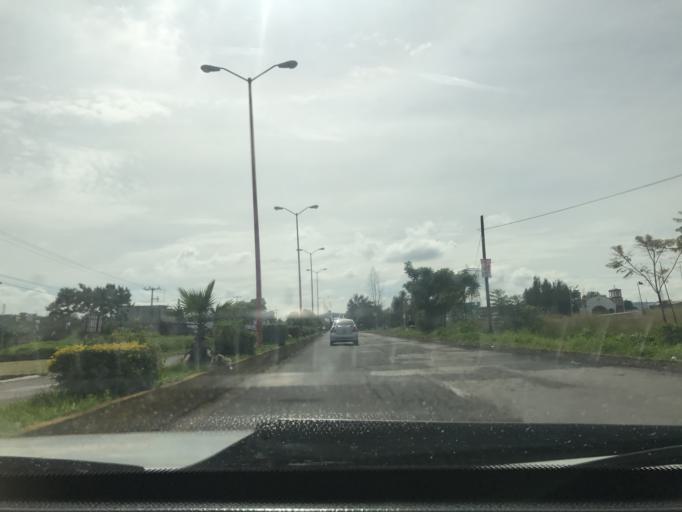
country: MX
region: Morelos
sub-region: Atlatlahucan
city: Colonia San Francisco
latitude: 18.8962
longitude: -98.9058
